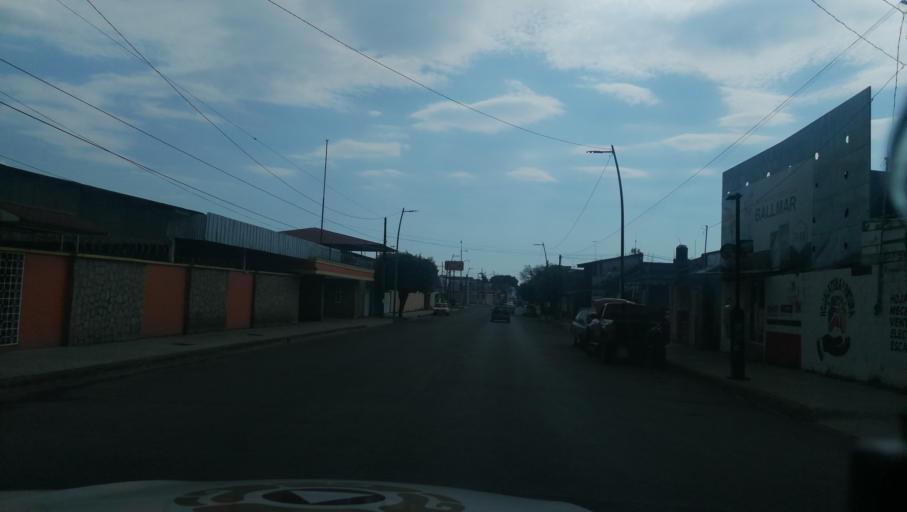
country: MX
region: Chiapas
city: Tapachula
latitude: 14.9223
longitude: -92.2547
